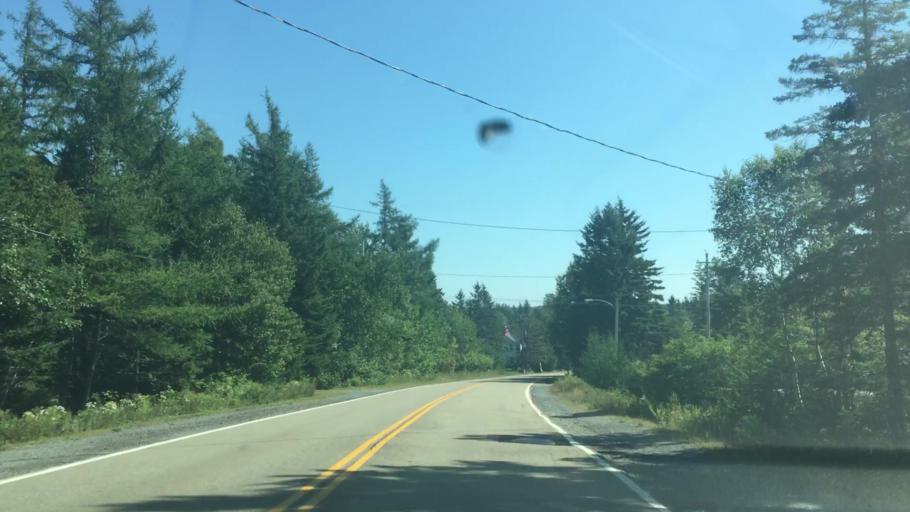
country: CA
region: Nova Scotia
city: Antigonish
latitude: 45.1445
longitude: -61.9873
